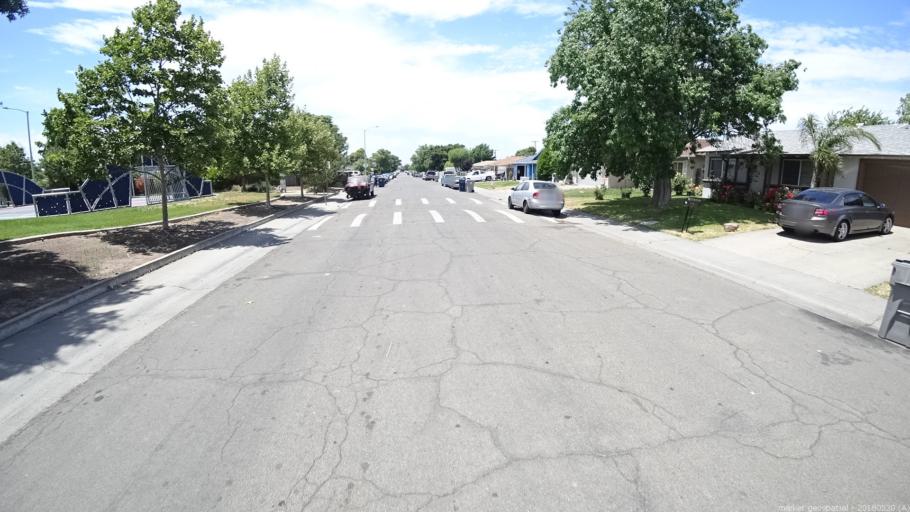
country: US
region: California
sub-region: Sacramento County
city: Sacramento
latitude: 38.6253
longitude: -121.4629
